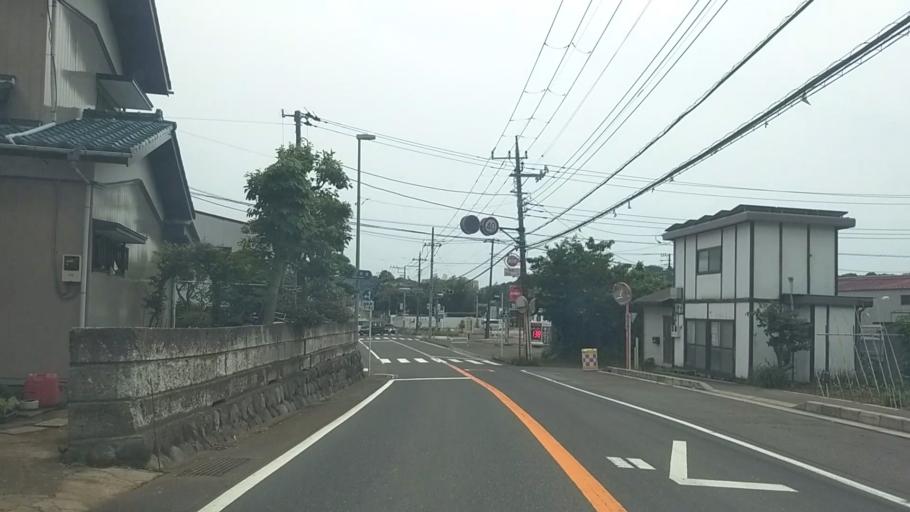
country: JP
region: Kanagawa
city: Chigasaki
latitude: 35.3660
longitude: 139.4216
